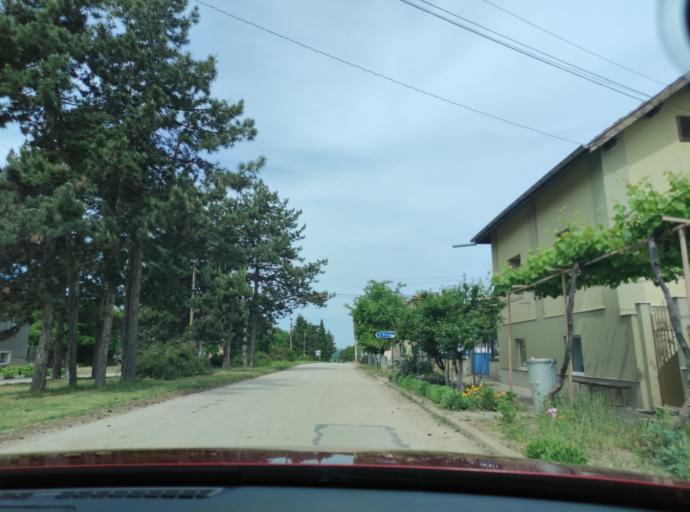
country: BG
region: Pleven
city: Iskur
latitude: 43.5368
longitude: 24.2844
